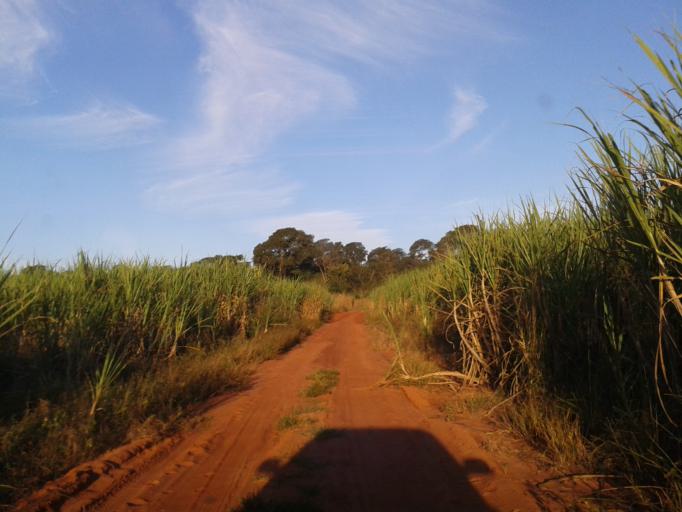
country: BR
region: Minas Gerais
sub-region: Santa Vitoria
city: Santa Vitoria
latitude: -19.0063
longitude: -50.3795
